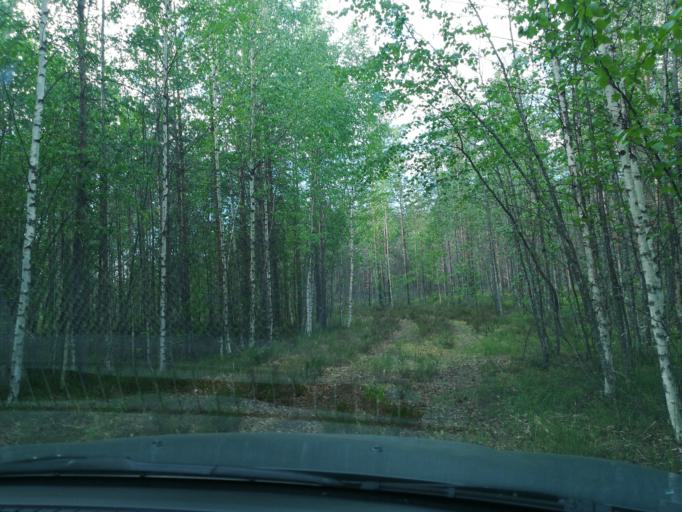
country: FI
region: Southern Savonia
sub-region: Savonlinna
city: Savonlinna
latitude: 61.6437
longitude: 28.7148
